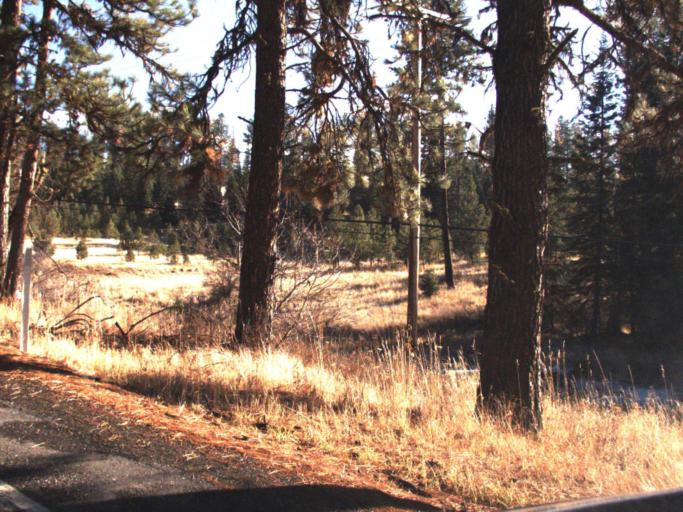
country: US
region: Washington
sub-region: Asotin County
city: Asotin
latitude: 46.0899
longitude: -117.1615
